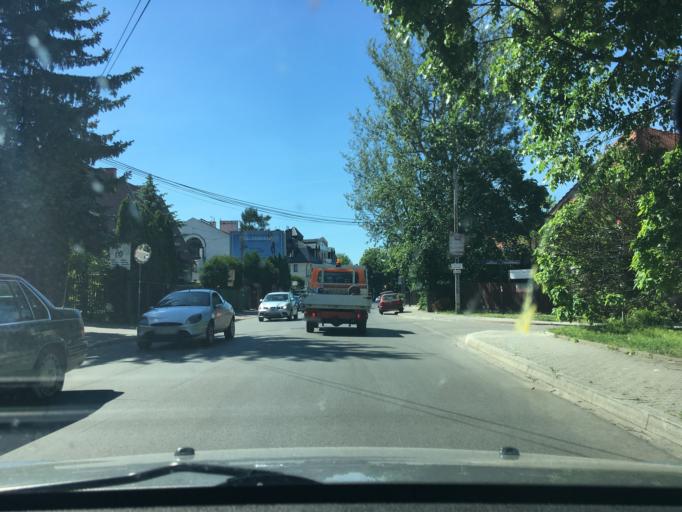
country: PL
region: Lesser Poland Voivodeship
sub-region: Krakow
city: Krakow
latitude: 50.0590
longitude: 19.8959
